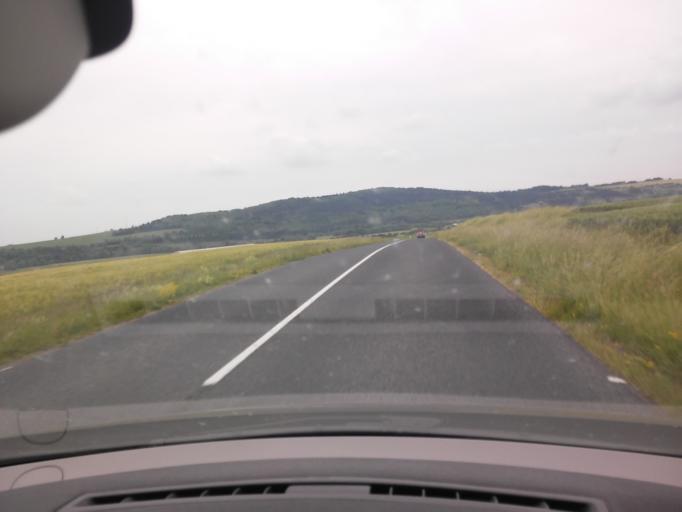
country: FR
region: Lorraine
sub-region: Departement de la Meuse
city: Saint-Mihiel
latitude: 48.8567
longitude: 5.5217
